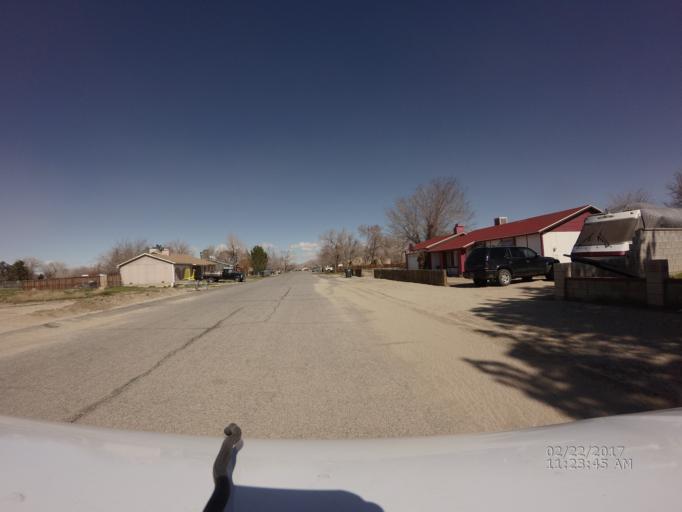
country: US
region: California
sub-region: Los Angeles County
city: Lake Los Angeles
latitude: 34.6201
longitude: -117.8128
